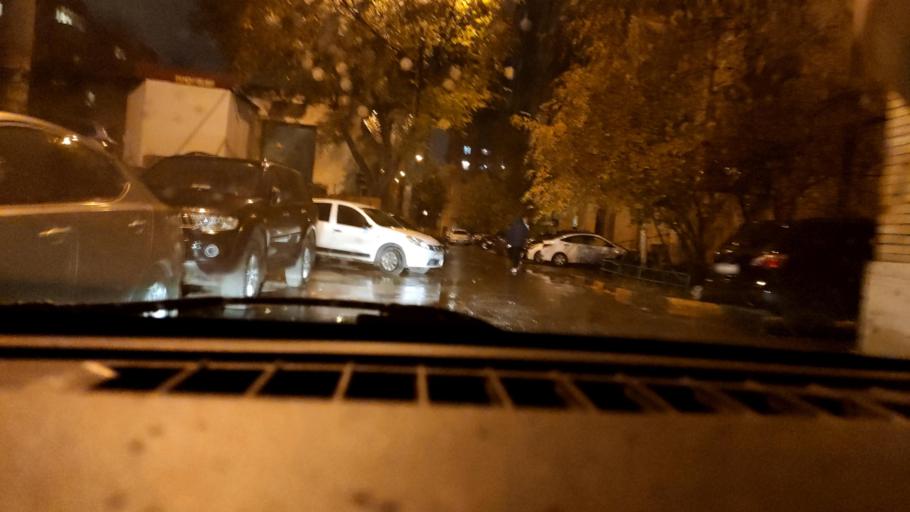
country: RU
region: Samara
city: Samara
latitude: 53.1932
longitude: 50.1991
